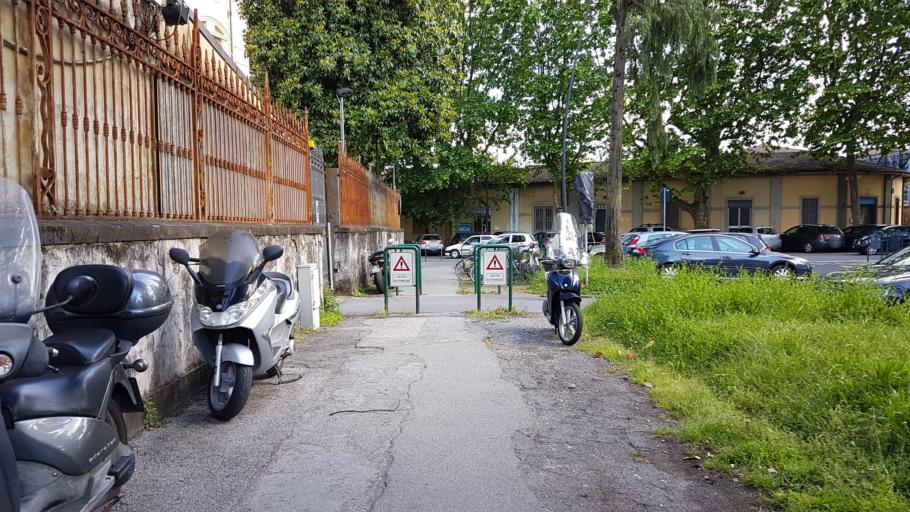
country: IT
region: Tuscany
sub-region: Provincia di Lucca
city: Lucca
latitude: 43.8381
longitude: 10.5038
